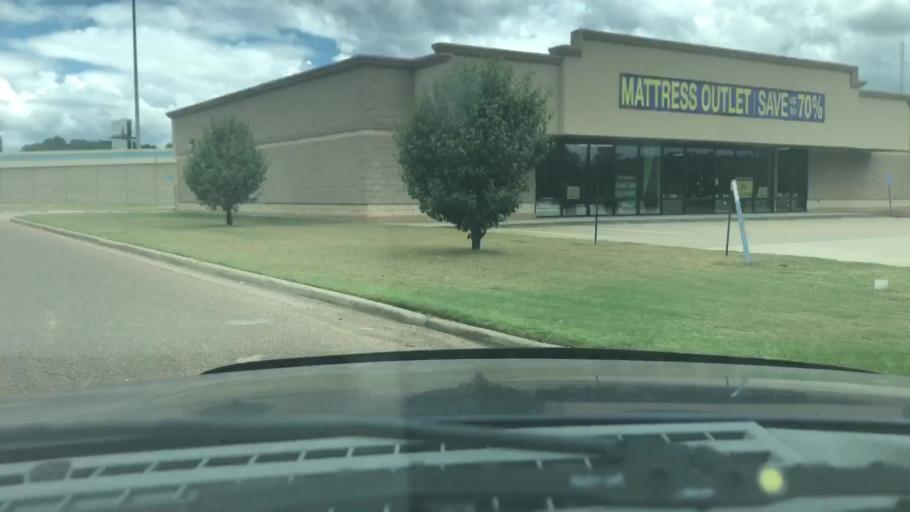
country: US
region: Texas
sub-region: Bowie County
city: Wake Village
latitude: 33.4483
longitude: -94.0982
